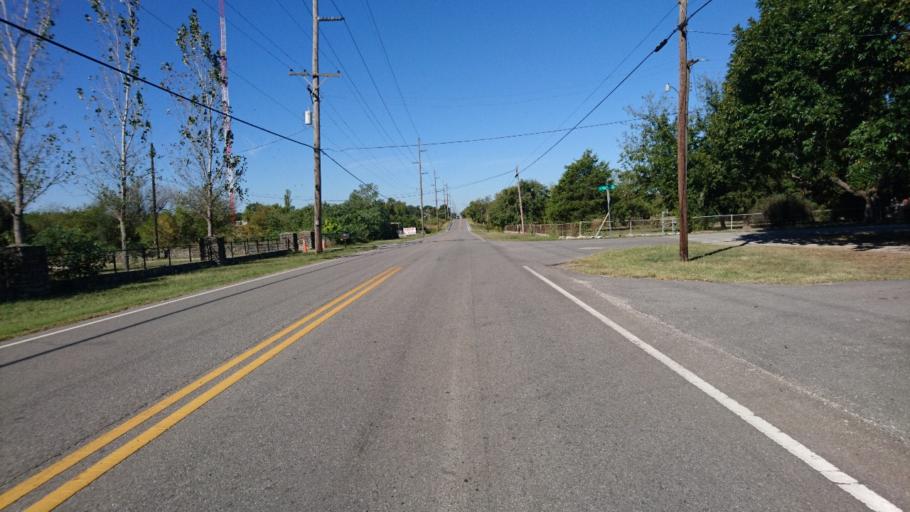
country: US
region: Oklahoma
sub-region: Rogers County
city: Catoosa
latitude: 36.1480
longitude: -95.8032
